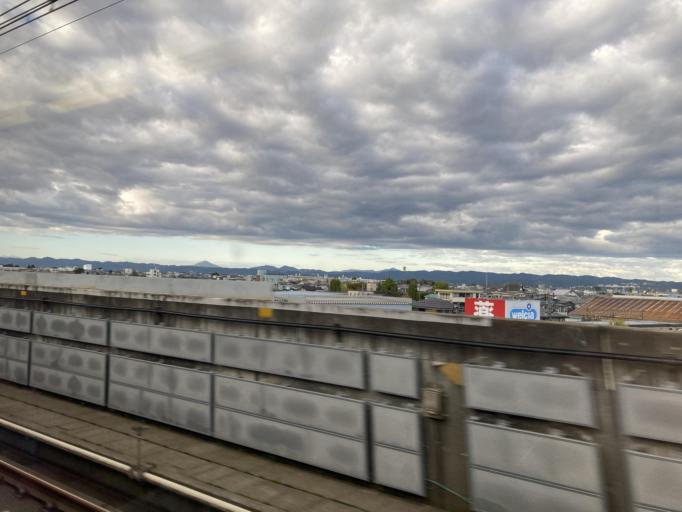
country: JP
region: Niigata
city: Nagaoka
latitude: 37.4294
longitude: 138.8497
